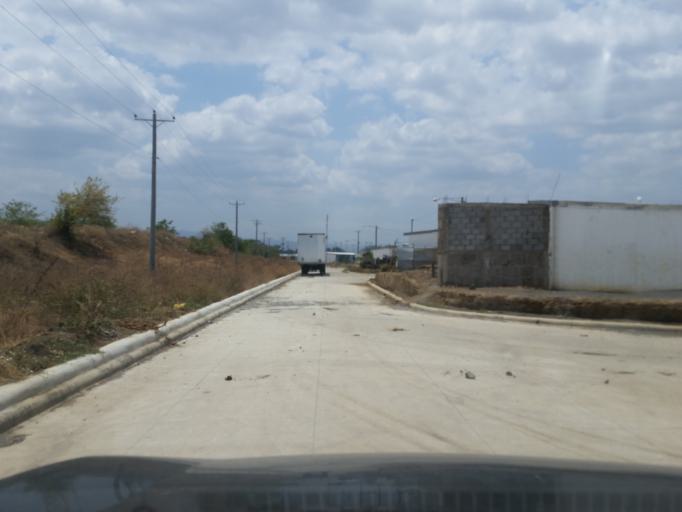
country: NI
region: Managua
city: Tipitapa
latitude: 12.1332
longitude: -86.1542
